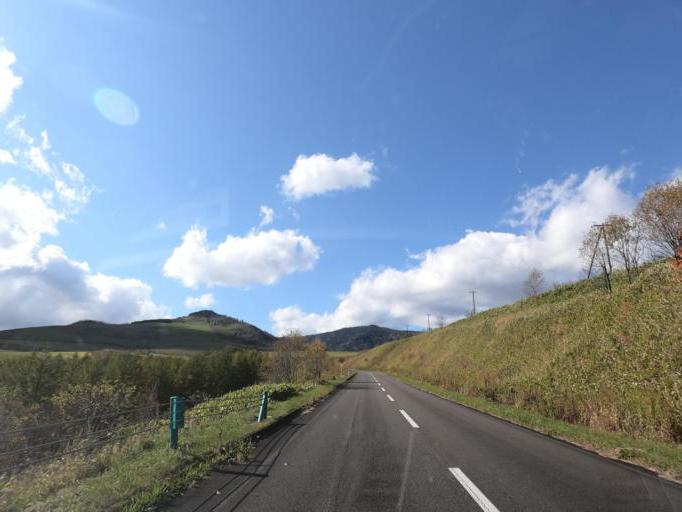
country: JP
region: Hokkaido
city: Otofuke
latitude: 43.2928
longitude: 143.1965
